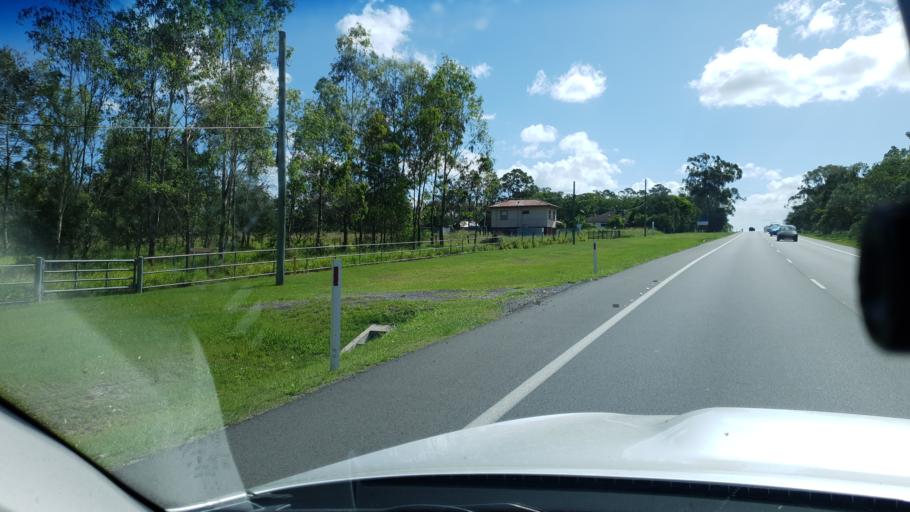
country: AU
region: Queensland
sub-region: Logan
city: Woodridge
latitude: -27.6500
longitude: 153.0835
